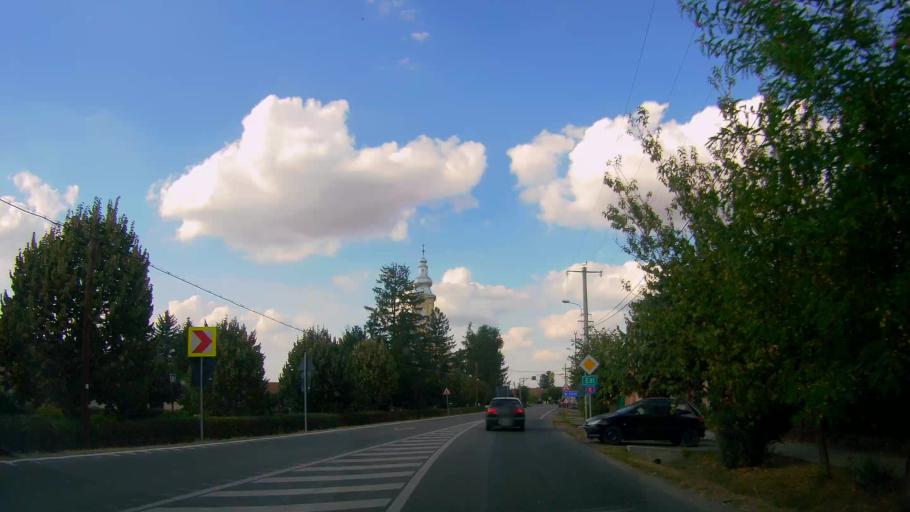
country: RO
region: Satu Mare
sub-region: Comuna Turulung
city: Turulung
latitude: 47.9334
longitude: 23.0829
